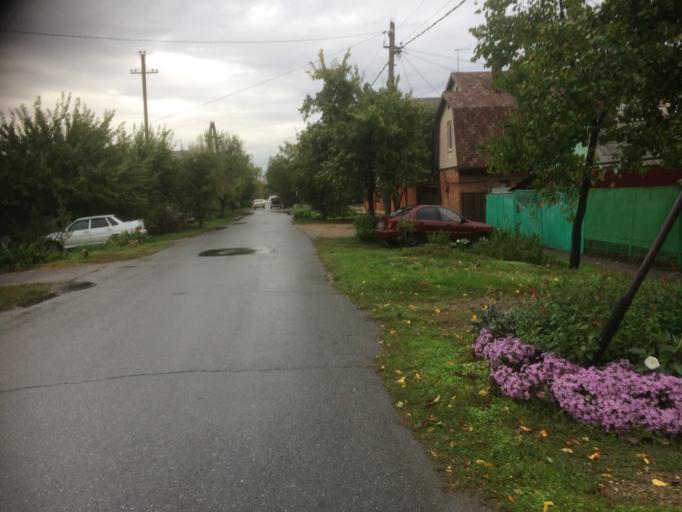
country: RU
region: Krasnodarskiy
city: Krasnodar
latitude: 45.0406
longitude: 38.9381
